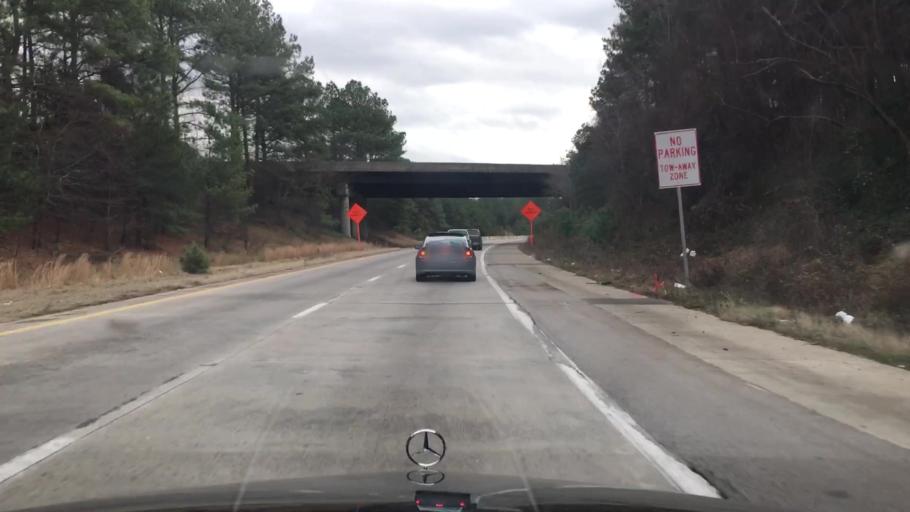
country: US
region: North Carolina
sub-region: Wake County
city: Raleigh
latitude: 35.7534
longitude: -78.5973
